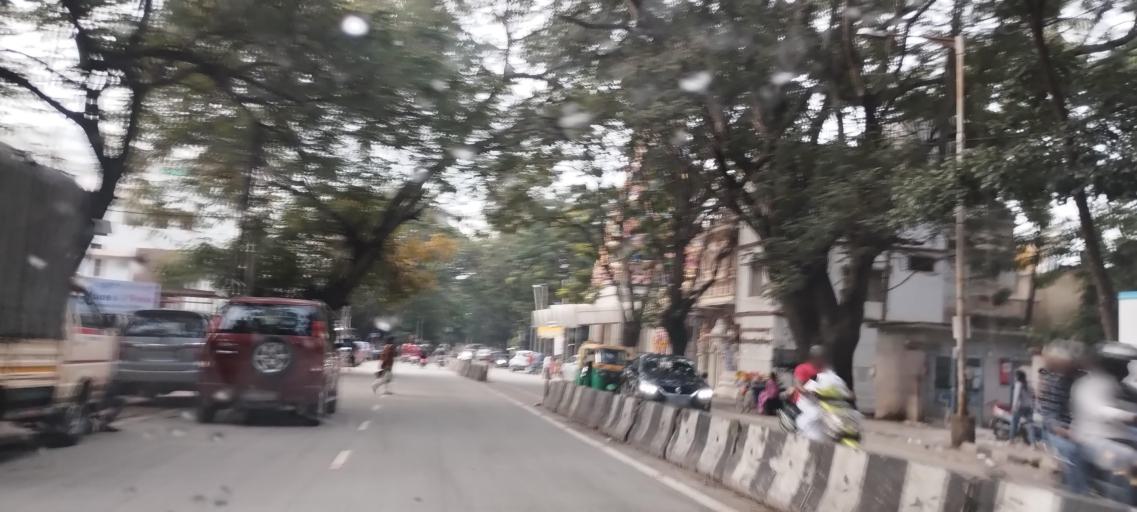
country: IN
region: Karnataka
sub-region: Bangalore Urban
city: Bangalore
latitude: 12.9502
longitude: 77.5768
